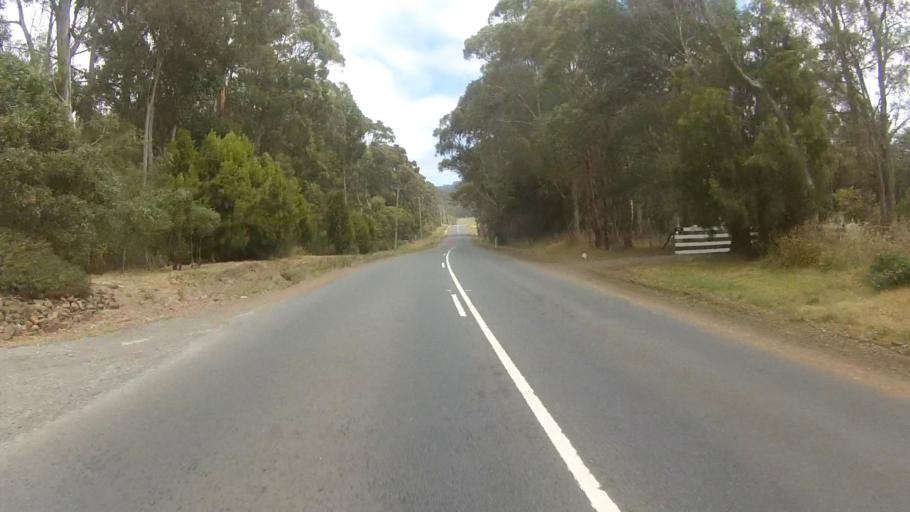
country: AU
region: Tasmania
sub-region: Kingborough
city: Margate
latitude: -42.9933
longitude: 147.2088
